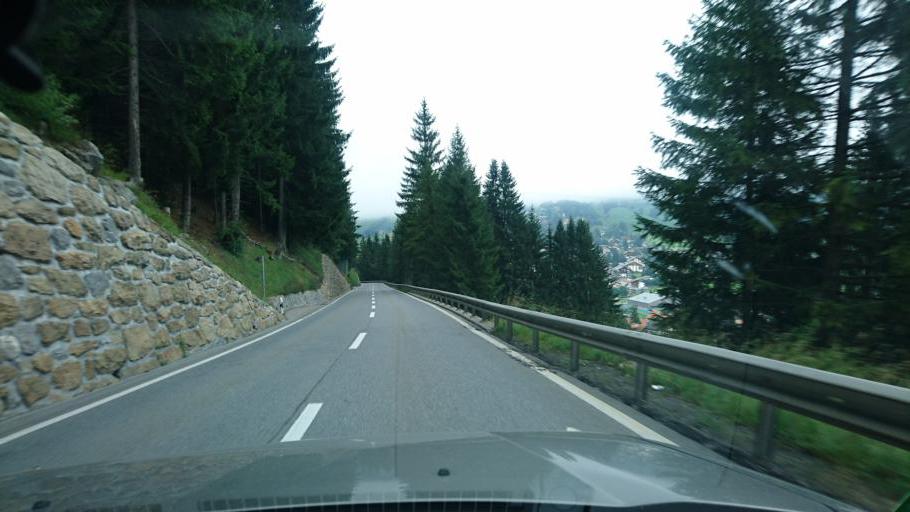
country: CH
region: Grisons
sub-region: Praettigau/Davos District
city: Klosters Serneus
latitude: 46.8619
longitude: 9.8789
